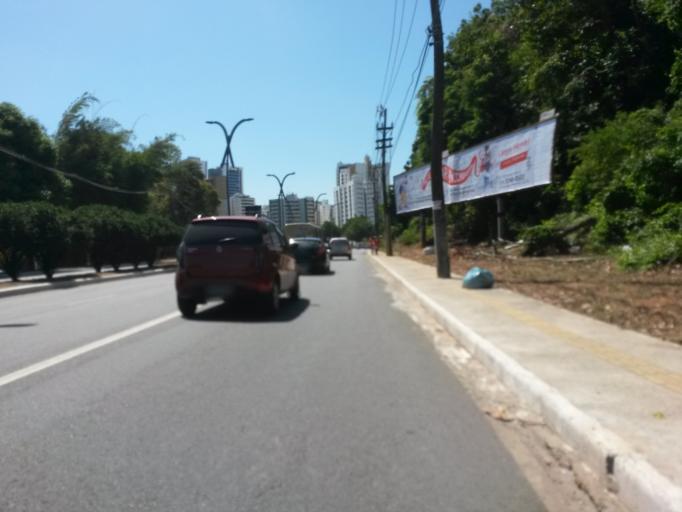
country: BR
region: Bahia
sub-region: Salvador
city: Salvador
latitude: -12.9958
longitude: -38.4733
